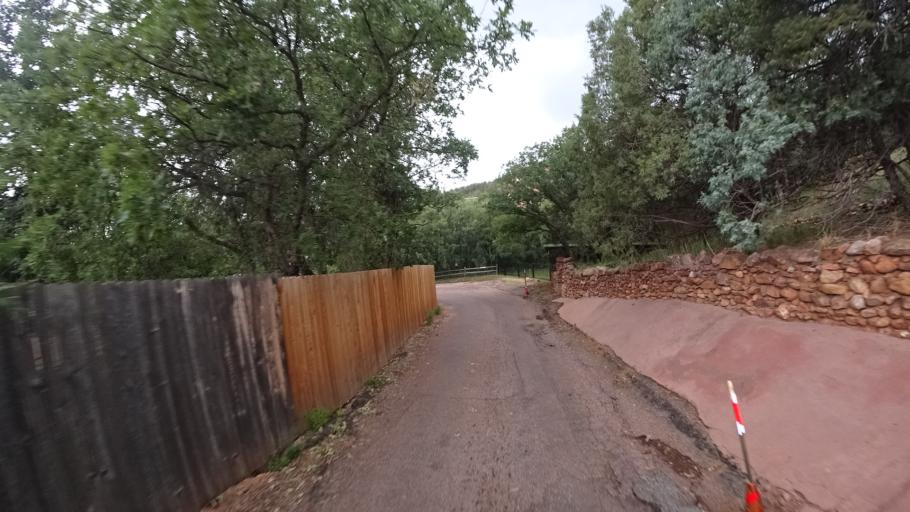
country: US
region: Colorado
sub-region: El Paso County
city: Manitou Springs
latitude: 38.8517
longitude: -104.8981
